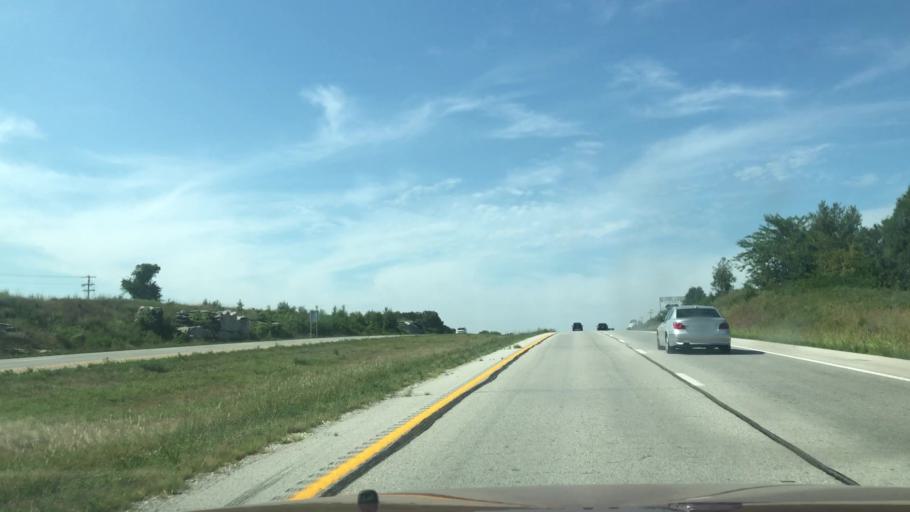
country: US
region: Missouri
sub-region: Christian County
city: Ozark
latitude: 36.9963
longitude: -93.2300
